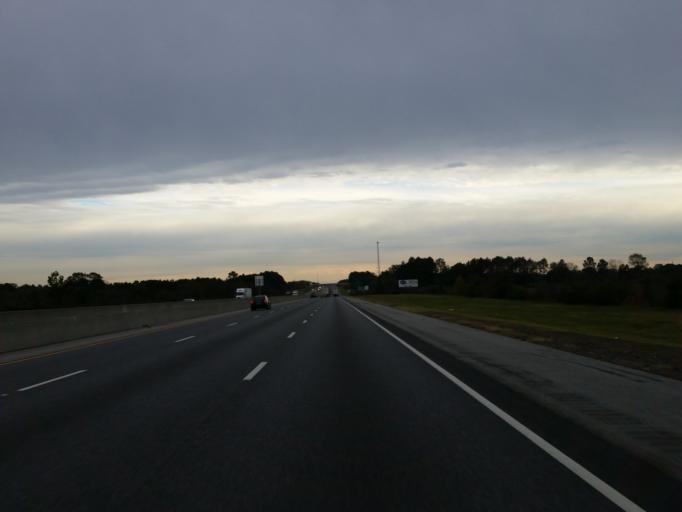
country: US
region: Georgia
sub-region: Turner County
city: Ashburn
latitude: 31.6594
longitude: -83.6029
